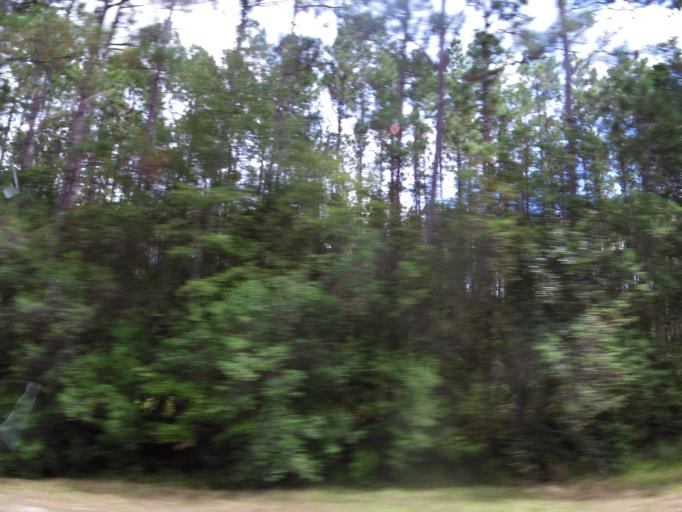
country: US
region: Georgia
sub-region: Brantley County
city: Nahunta
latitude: 31.1361
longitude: -81.9959
